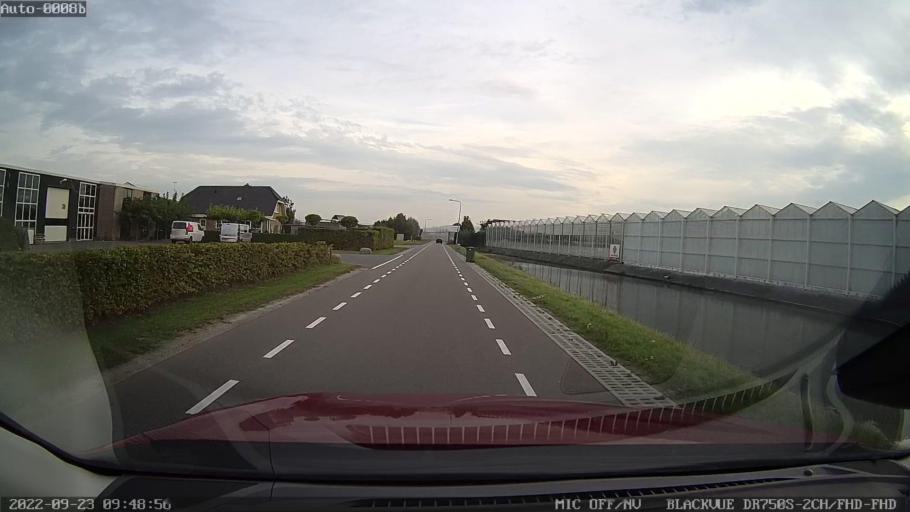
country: NL
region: South Holland
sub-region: Gemeente Westland
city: Kwintsheul
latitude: 51.9959
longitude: 4.2528
